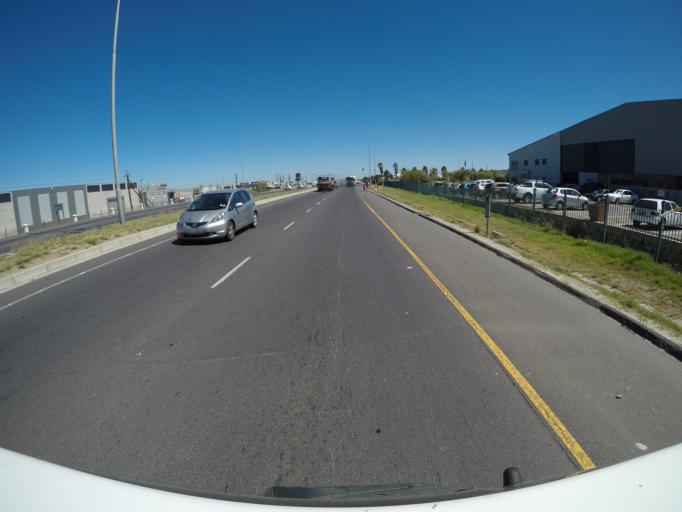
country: ZA
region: Western Cape
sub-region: Overberg District Municipality
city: Grabouw
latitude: -34.1044
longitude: 18.8556
